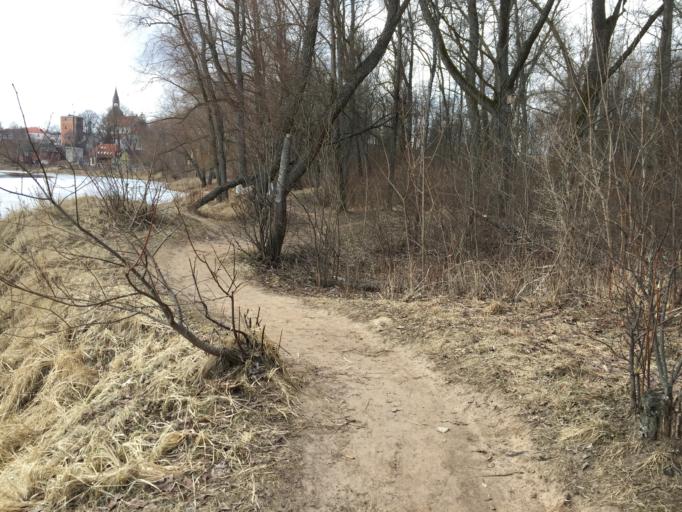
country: LV
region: Valmieras Rajons
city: Valmiera
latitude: 57.5376
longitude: 25.4338
